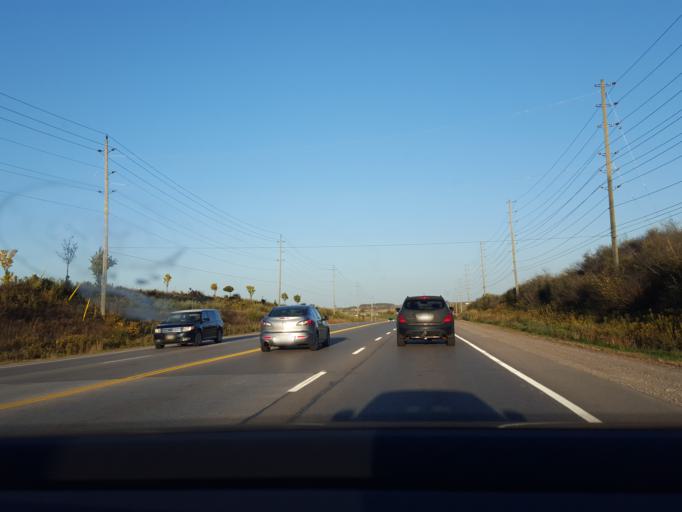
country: CA
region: Ontario
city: Newmarket
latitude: 44.0745
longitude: -79.4773
